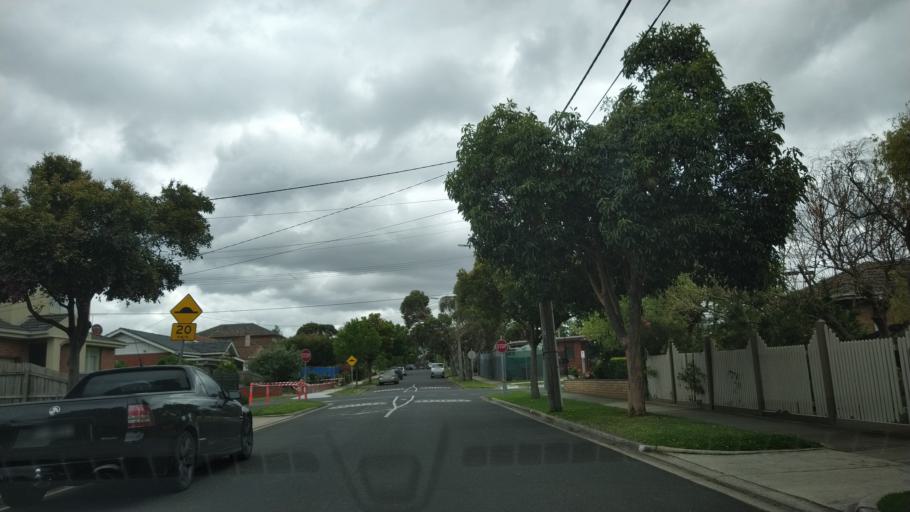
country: AU
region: Victoria
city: Ormond
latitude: -37.8997
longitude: 145.0375
